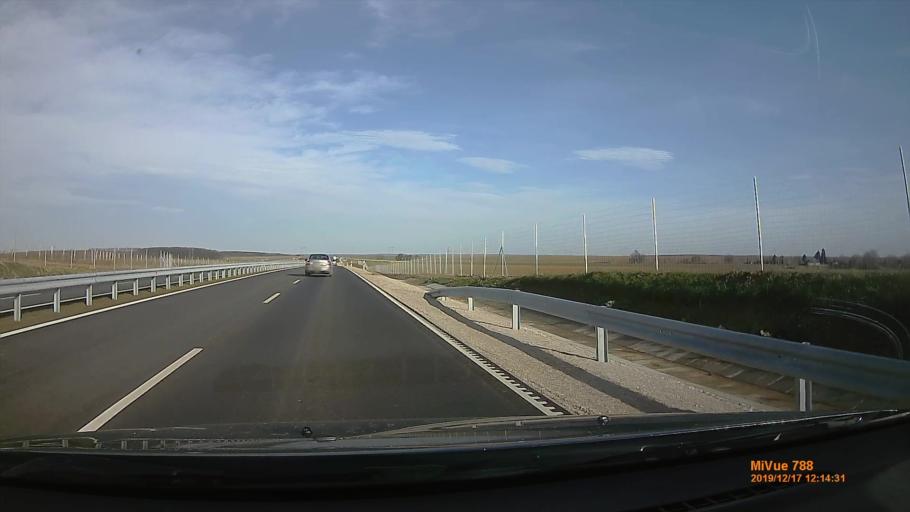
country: HU
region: Somogy
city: Kaposvar
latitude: 46.4653
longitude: 17.7946
